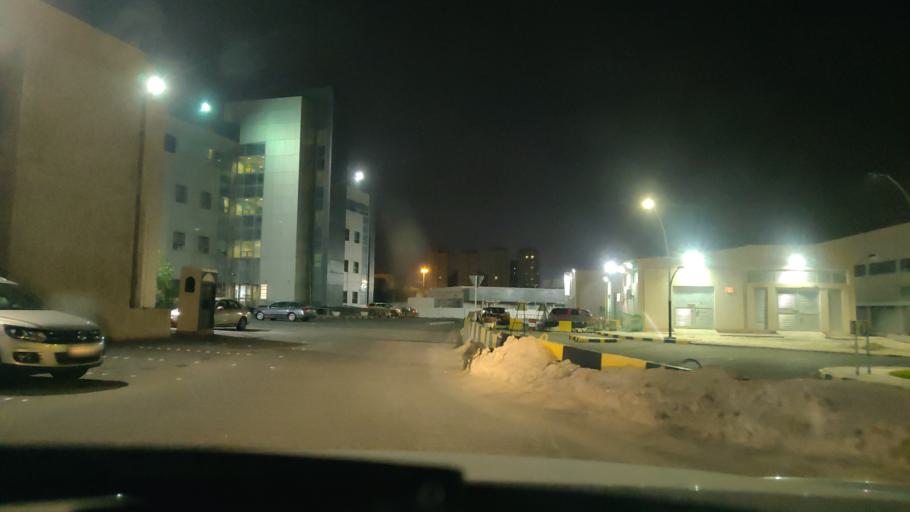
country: KW
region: Muhafazat al Jahra'
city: Al Jahra'
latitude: 29.3384
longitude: 47.6800
